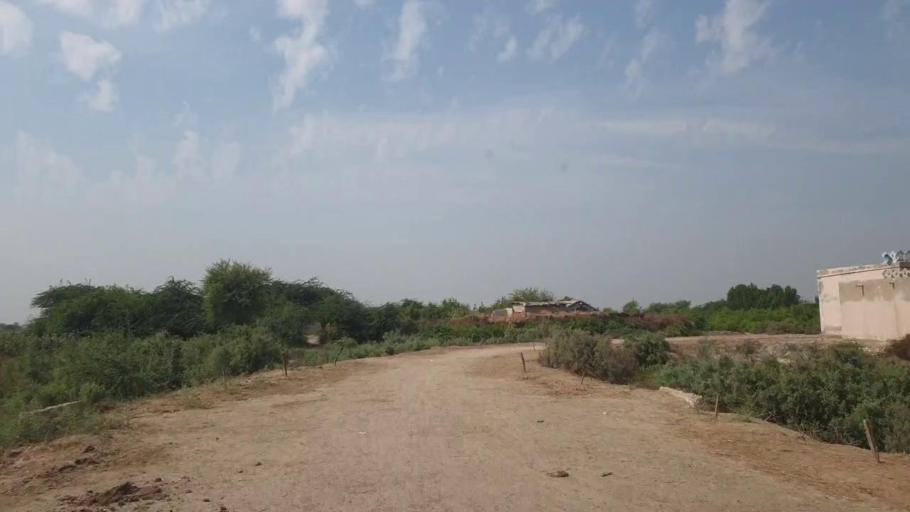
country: PK
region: Sindh
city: Rajo Khanani
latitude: 24.9887
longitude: 68.9763
